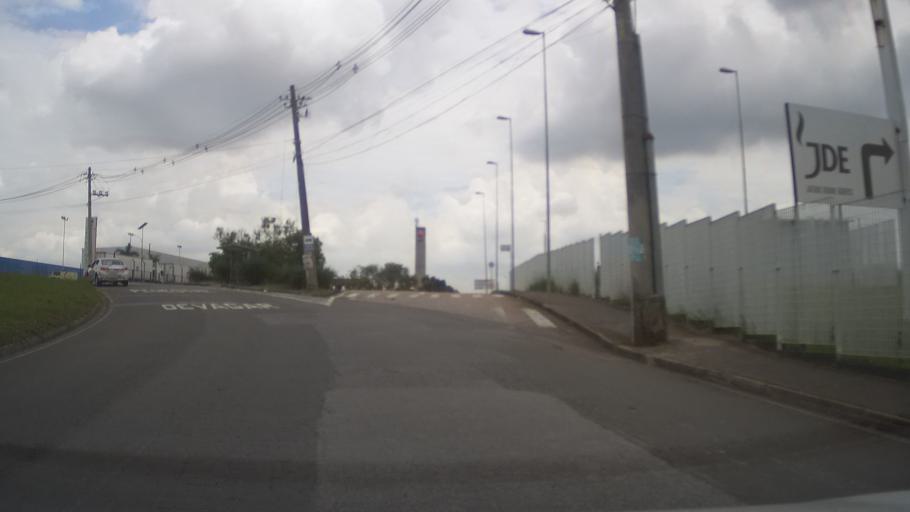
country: BR
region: Sao Paulo
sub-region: Itupeva
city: Itupeva
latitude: -23.1600
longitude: -47.0024
